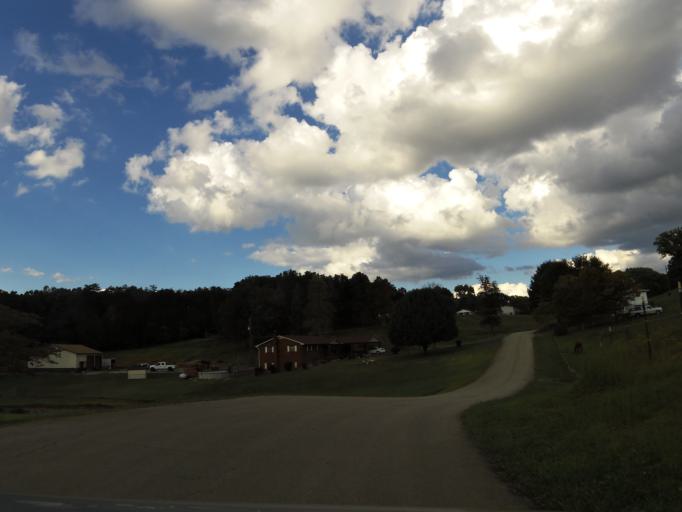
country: US
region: Tennessee
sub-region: Knox County
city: Mascot
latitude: 36.1130
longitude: -83.7809
